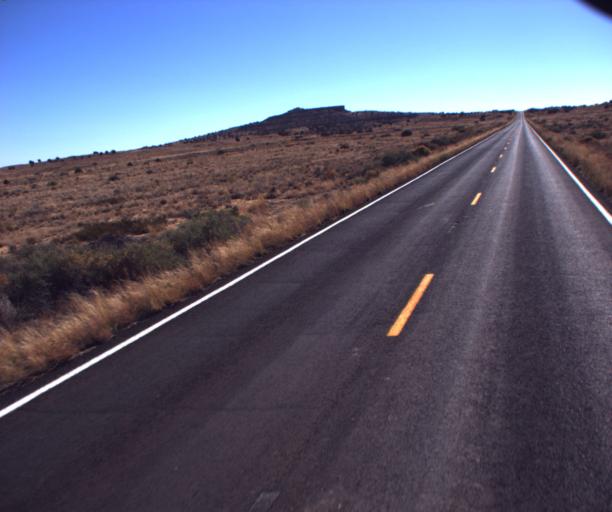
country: US
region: Arizona
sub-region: Navajo County
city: First Mesa
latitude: 35.9689
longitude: -110.6935
